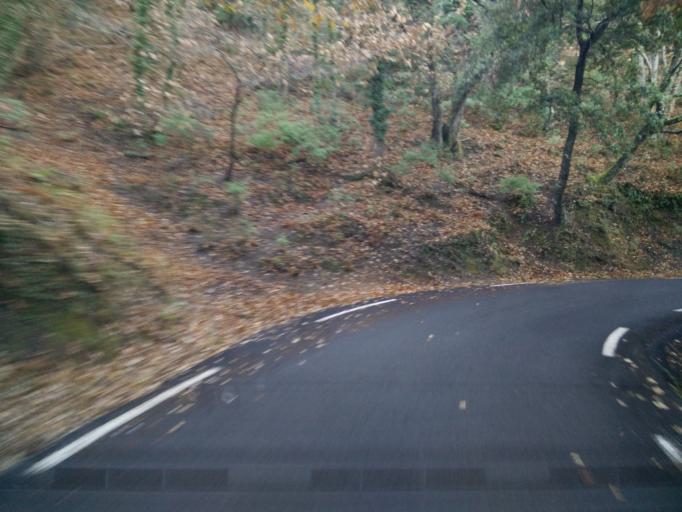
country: FR
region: Provence-Alpes-Cote d'Azur
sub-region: Departement du Var
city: Collobrieres
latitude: 43.2396
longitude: 6.3380
